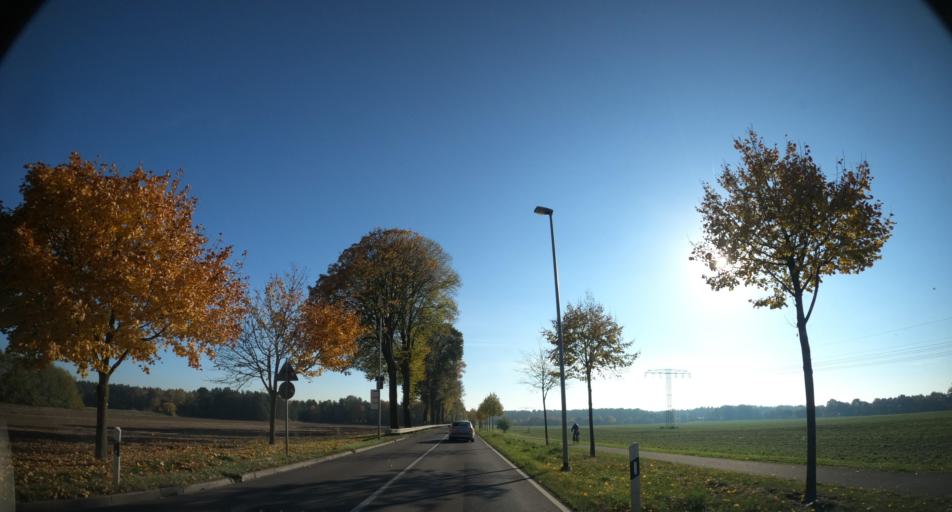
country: DE
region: Mecklenburg-Vorpommern
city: Ueckermunde
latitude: 53.7203
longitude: 14.0631
